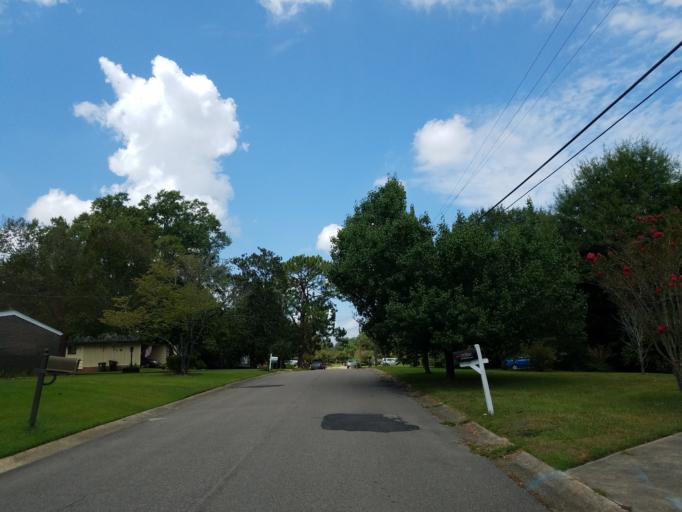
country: US
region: Mississippi
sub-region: Lamar County
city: West Hattiesburg
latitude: 31.3119
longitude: -89.3347
